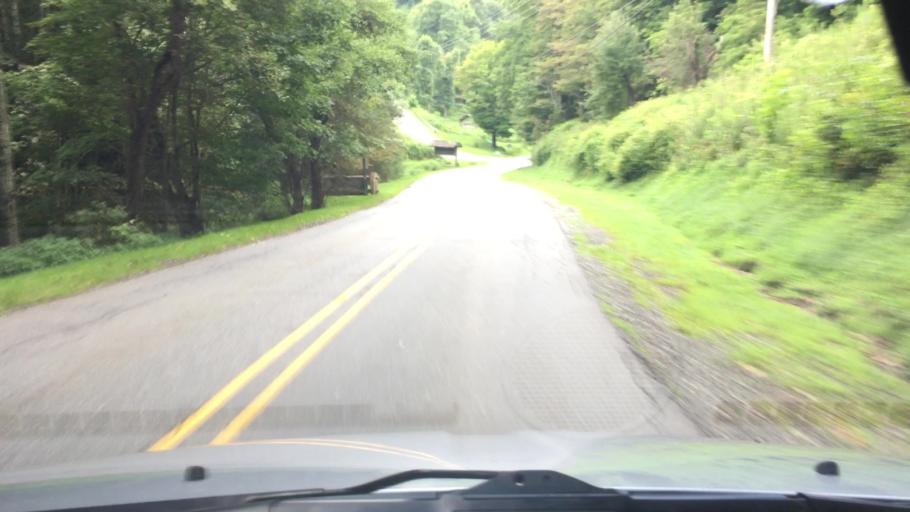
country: US
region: North Carolina
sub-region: Madison County
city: Mars Hill
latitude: 35.9523
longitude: -82.5173
